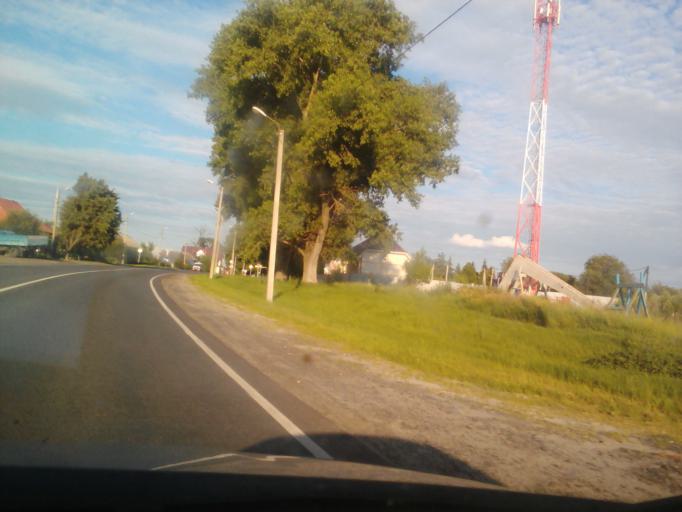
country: RU
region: Kursk
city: Kurchatov
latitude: 51.6675
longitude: 35.7389
